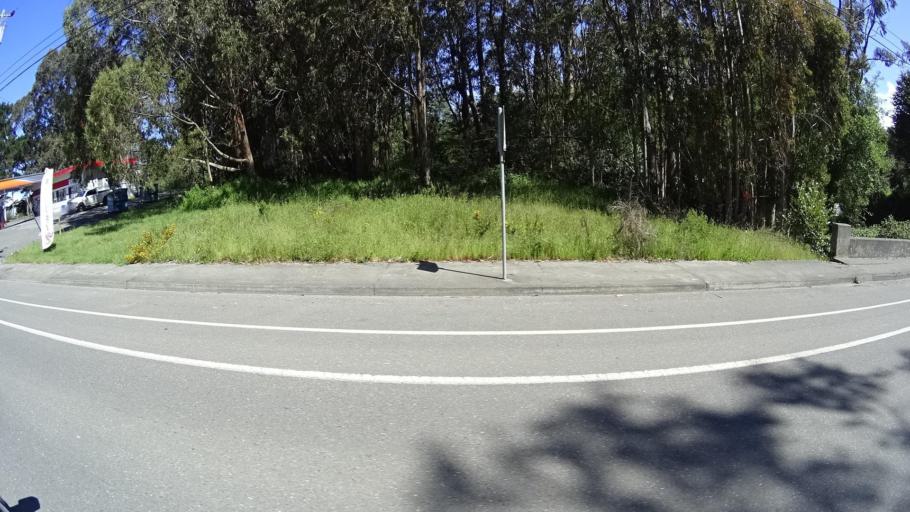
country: US
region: California
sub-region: Humboldt County
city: McKinleyville
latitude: 40.9563
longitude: -124.1142
